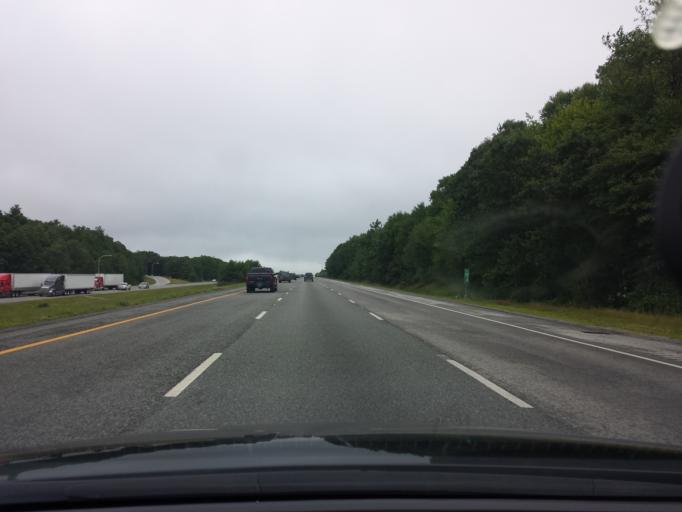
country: US
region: Rhode Island
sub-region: Washington County
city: Hope Valley
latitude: 41.5536
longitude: -71.6708
